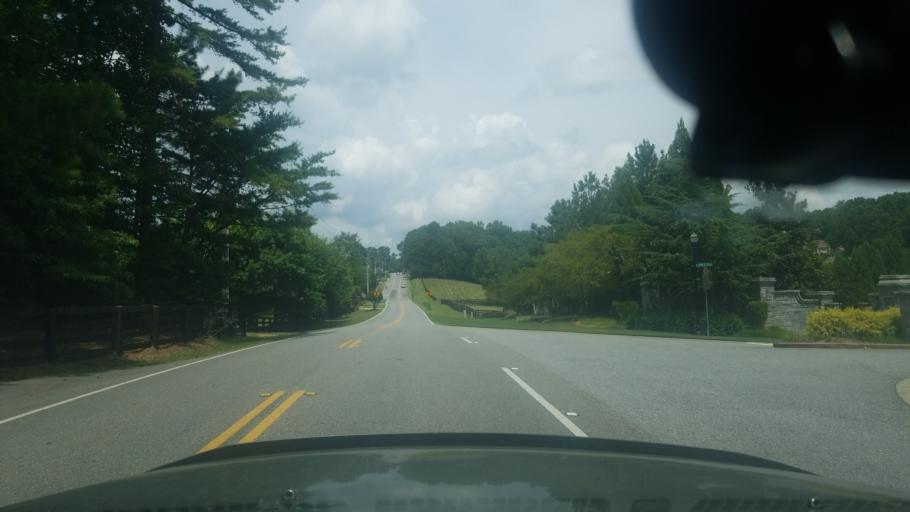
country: US
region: Georgia
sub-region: Fulton County
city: Johns Creek
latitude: 34.1043
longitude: -84.1587
